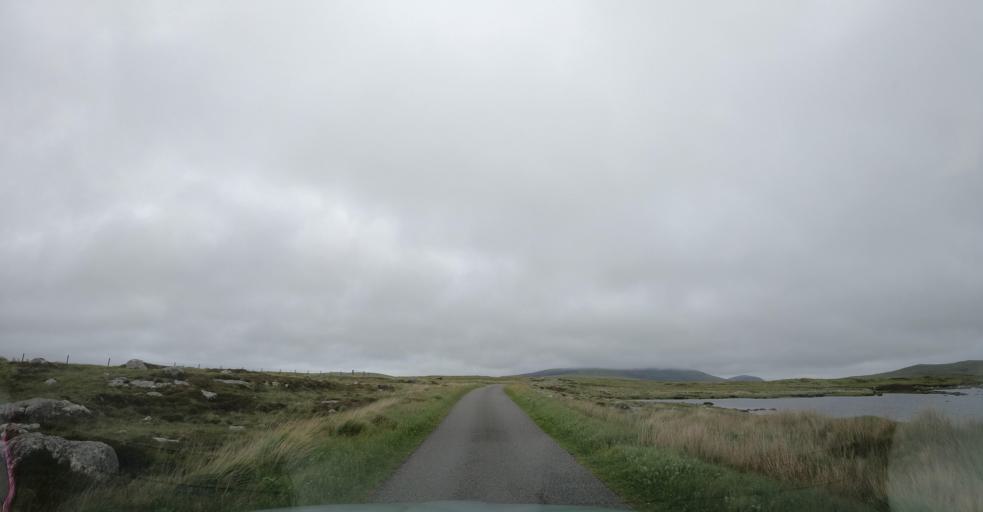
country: GB
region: Scotland
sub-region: Eilean Siar
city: Isle of North Uist
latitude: 57.5816
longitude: -7.4049
